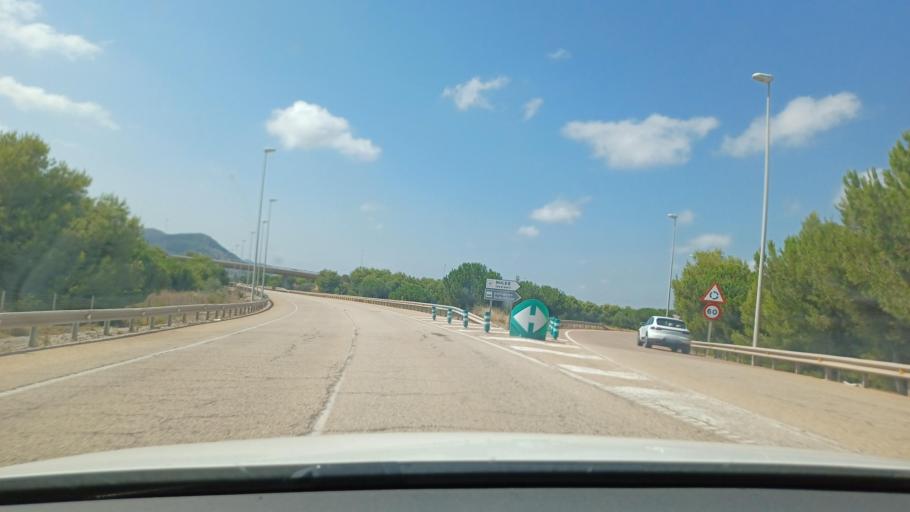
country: ES
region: Valencia
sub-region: Provincia de Castello
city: Nules
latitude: 39.8333
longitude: -0.1648
